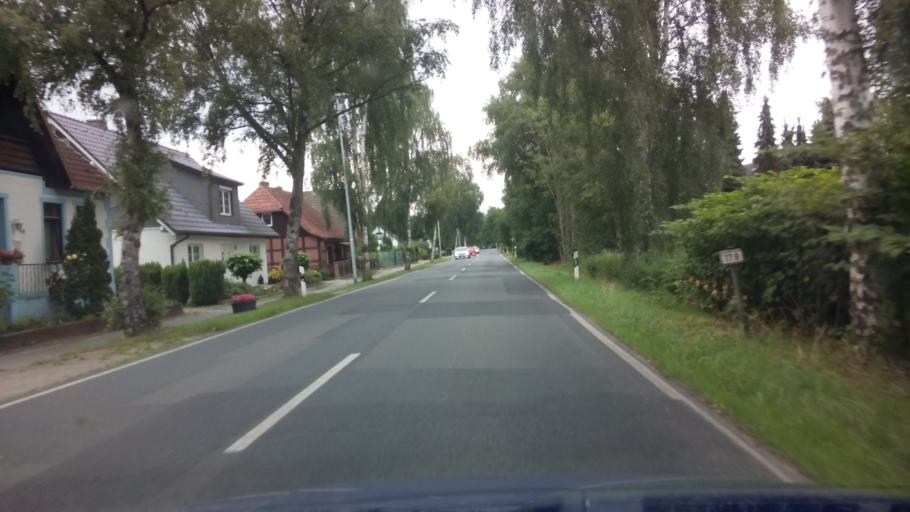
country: DE
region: Lower Saxony
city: Worpswede
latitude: 53.2043
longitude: 8.9314
